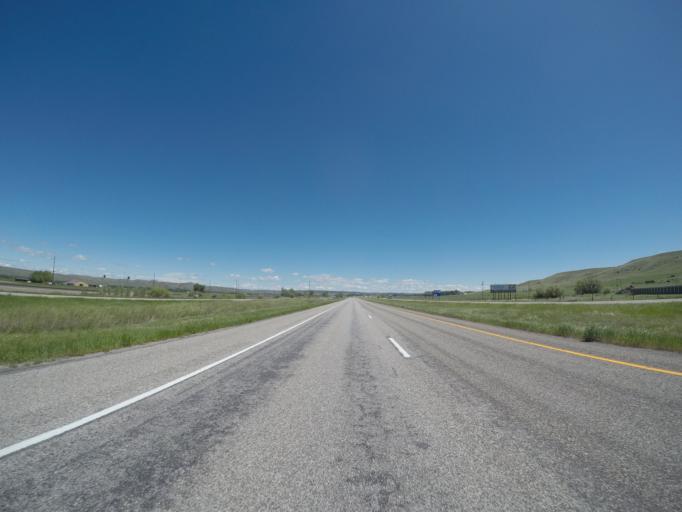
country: US
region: Montana
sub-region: Sweet Grass County
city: Big Timber
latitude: 45.8191
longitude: -109.9903
